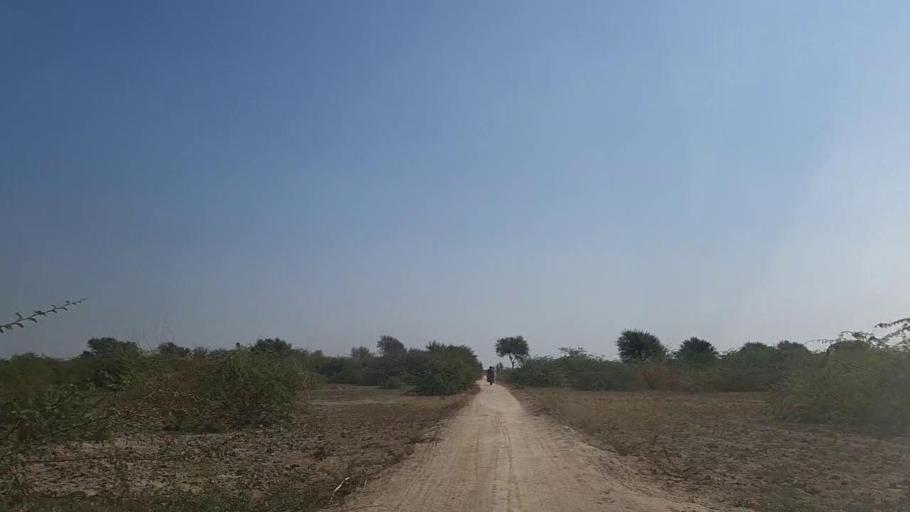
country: PK
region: Sindh
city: Digri
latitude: 25.1651
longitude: 69.1735
